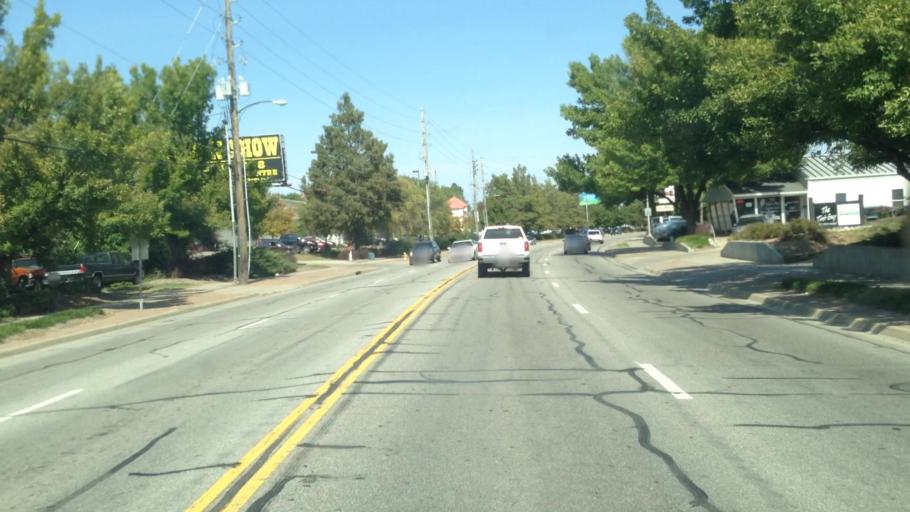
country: US
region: Kansas
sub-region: Douglas County
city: Lawrence
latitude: 38.9825
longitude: -95.2353
